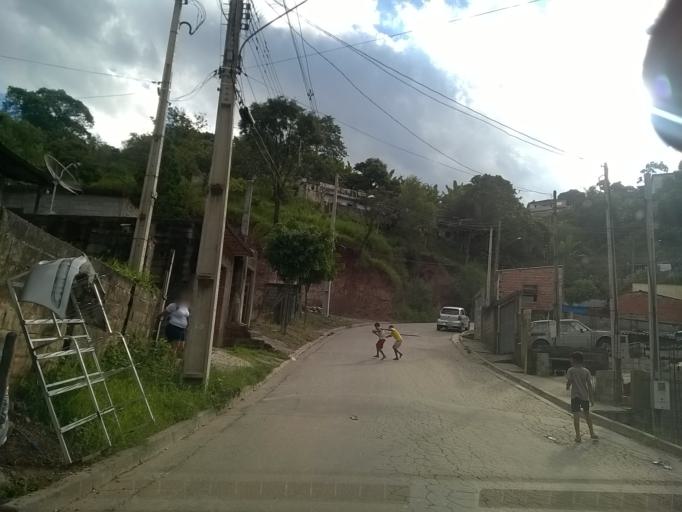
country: BR
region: Sao Paulo
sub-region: Francisco Morato
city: Francisco Morato
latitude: -23.2853
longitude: -46.7586
